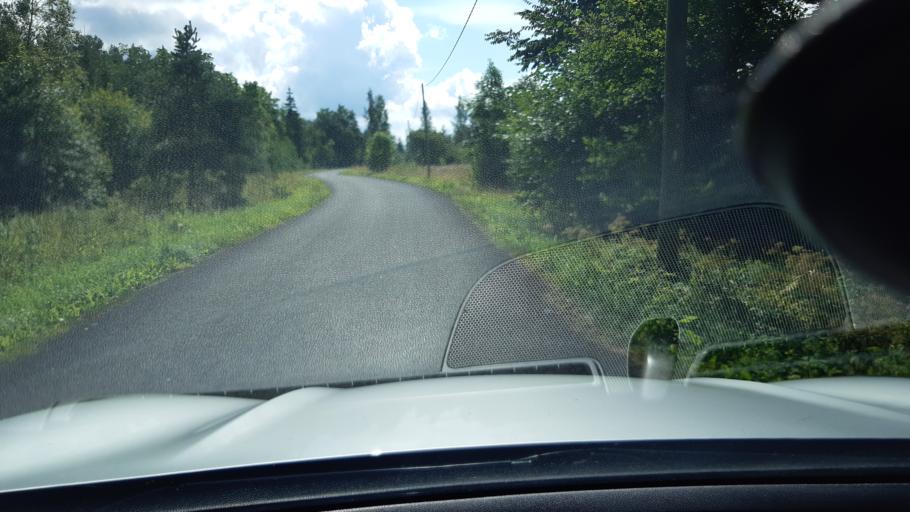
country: EE
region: Raplamaa
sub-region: Kehtna vald
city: Kehtna
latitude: 58.9378
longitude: 24.8965
